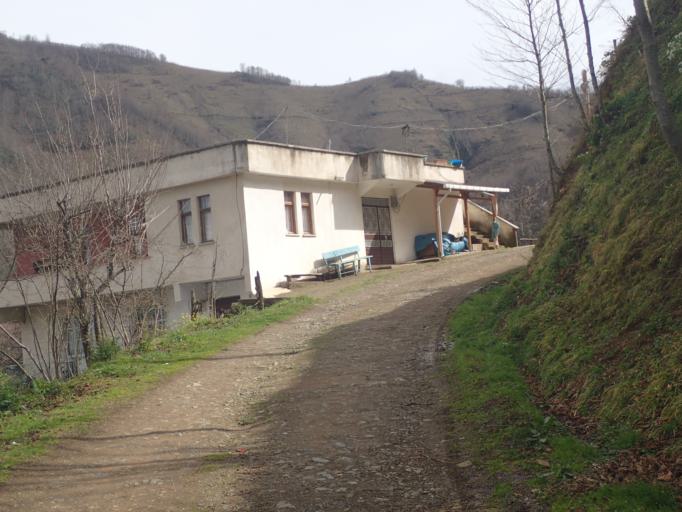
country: TR
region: Ordu
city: Camas
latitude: 40.8964
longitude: 37.5778
